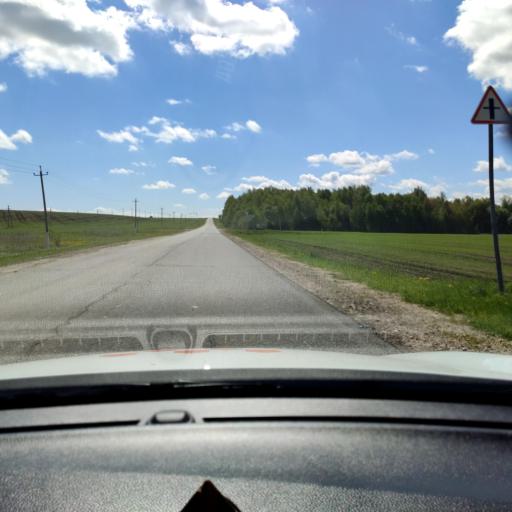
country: RU
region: Tatarstan
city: Verkhniy Uslon
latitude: 55.5815
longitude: 48.8892
